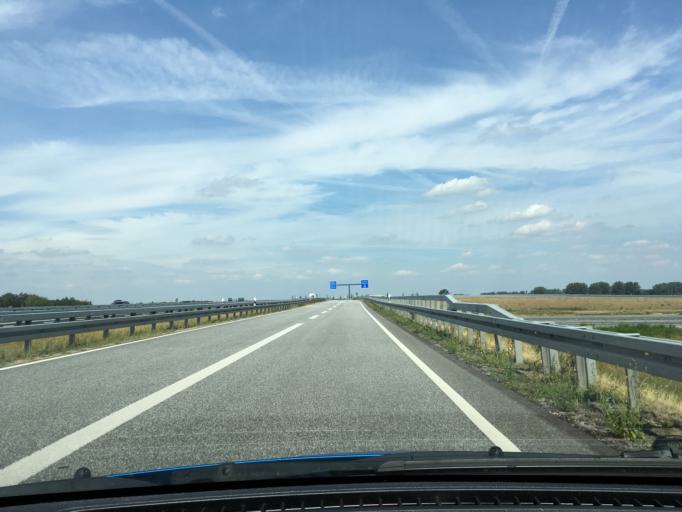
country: DE
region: Mecklenburg-Vorpommern
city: Gross Laasch
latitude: 53.4219
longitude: 11.5213
